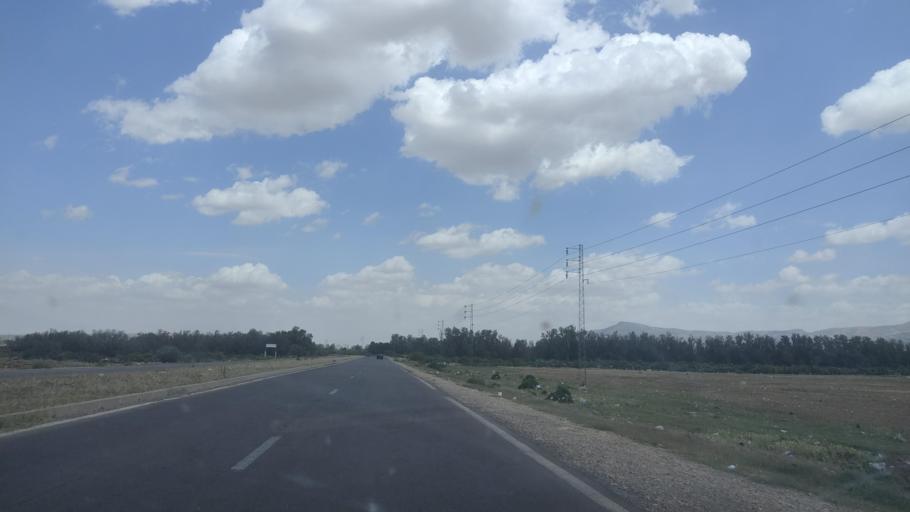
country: TN
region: Al Qasrayn
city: Kasserine
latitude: 35.1985
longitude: 8.8650
